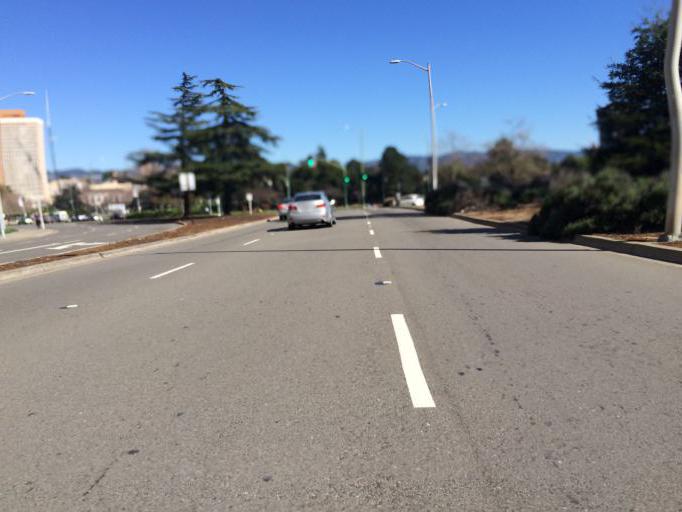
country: US
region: California
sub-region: Alameda County
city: Oakland
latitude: 37.8081
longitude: -122.2642
